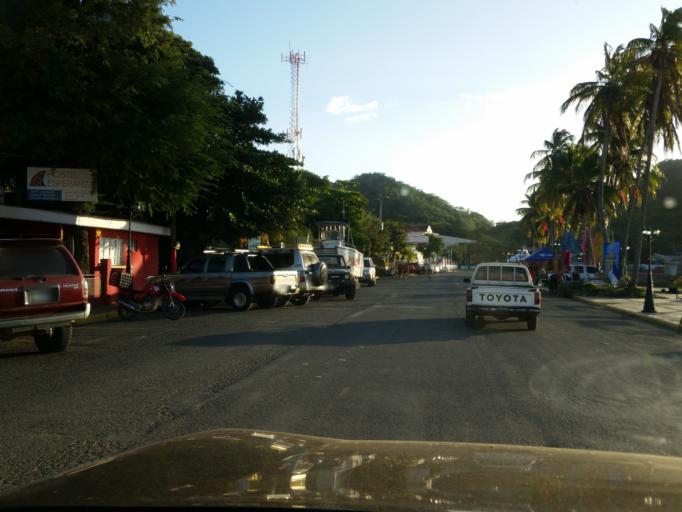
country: NI
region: Rivas
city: San Juan del Sur
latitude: 11.2520
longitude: -85.8725
